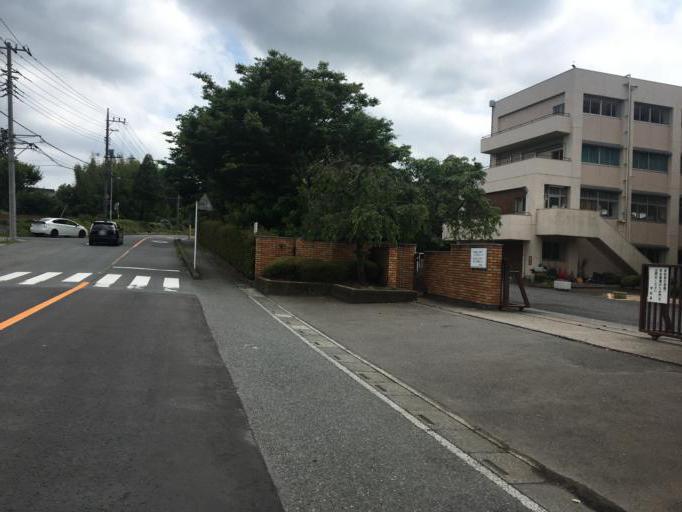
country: JP
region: Saitama
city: Okegawa
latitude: 35.9473
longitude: 139.5498
